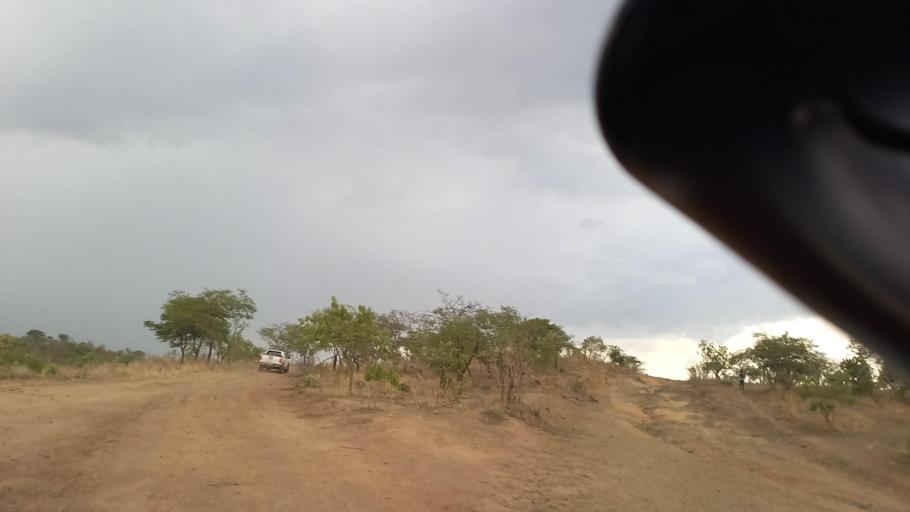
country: ZM
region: Lusaka
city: Kafue
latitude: -16.1240
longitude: 28.0616
